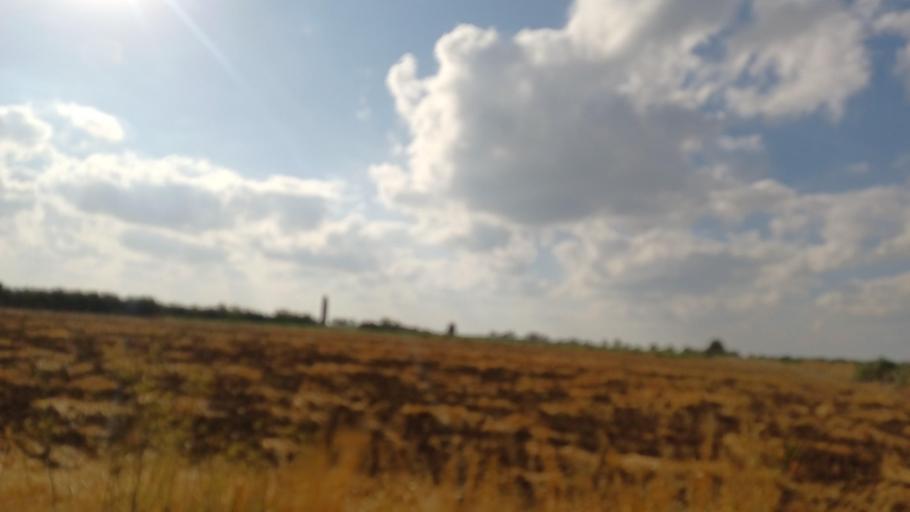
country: CY
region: Limassol
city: Pissouri
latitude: 34.7032
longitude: 32.5611
